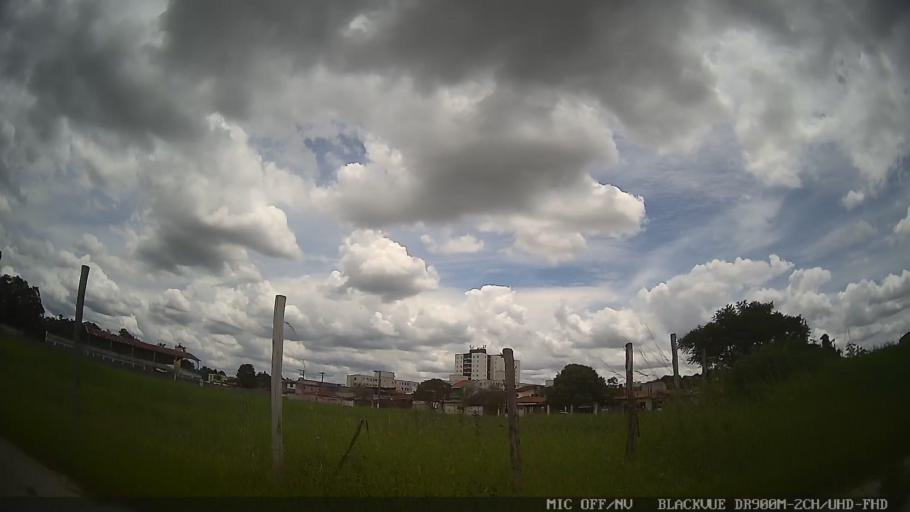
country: BR
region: Sao Paulo
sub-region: Suzano
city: Suzano
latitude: -23.5540
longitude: -46.3018
